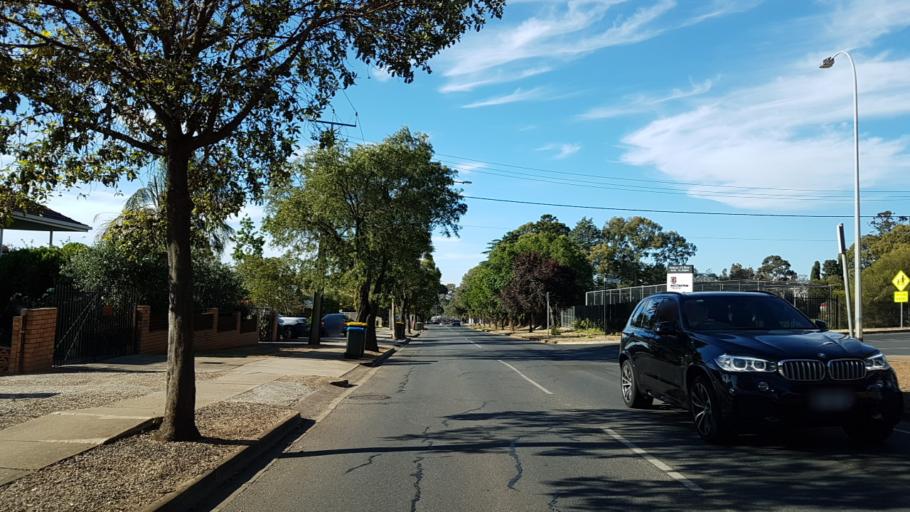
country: AU
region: South Australia
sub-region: Burnside
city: Wattle Park
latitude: -34.9042
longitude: 138.6844
